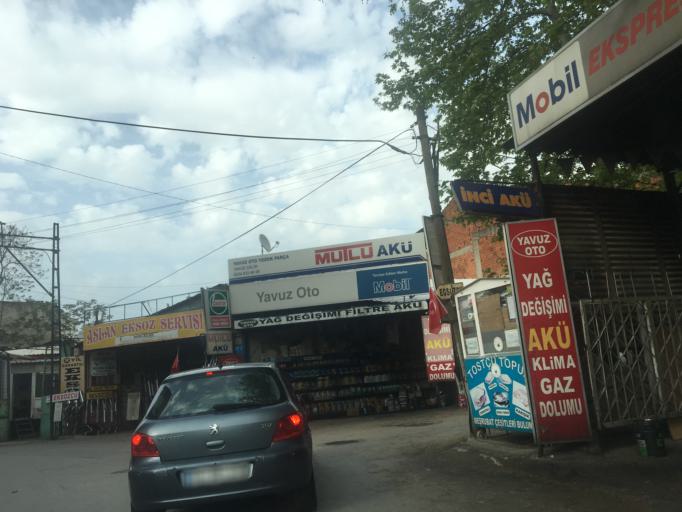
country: TR
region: Bursa
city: Yildirim
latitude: 40.2003
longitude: 29.0455
